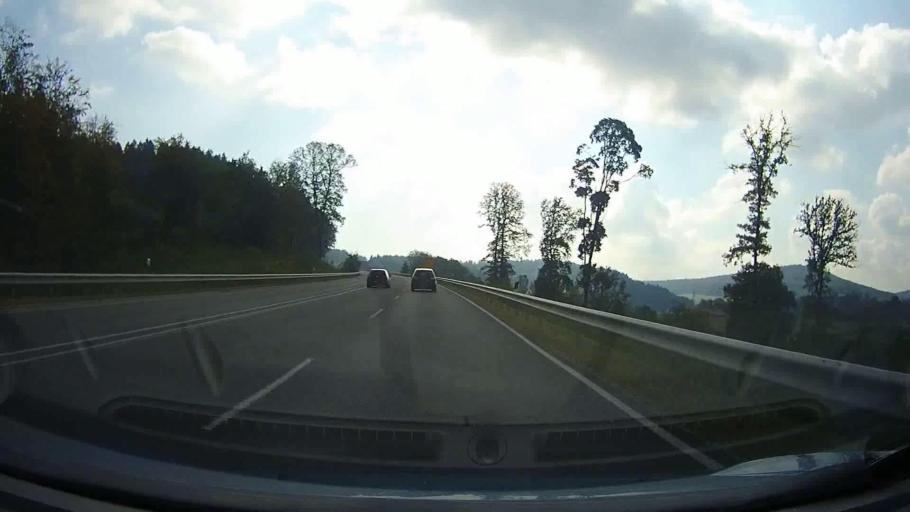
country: DE
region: Lower Saxony
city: Hardegsen
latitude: 51.6514
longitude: 9.7641
